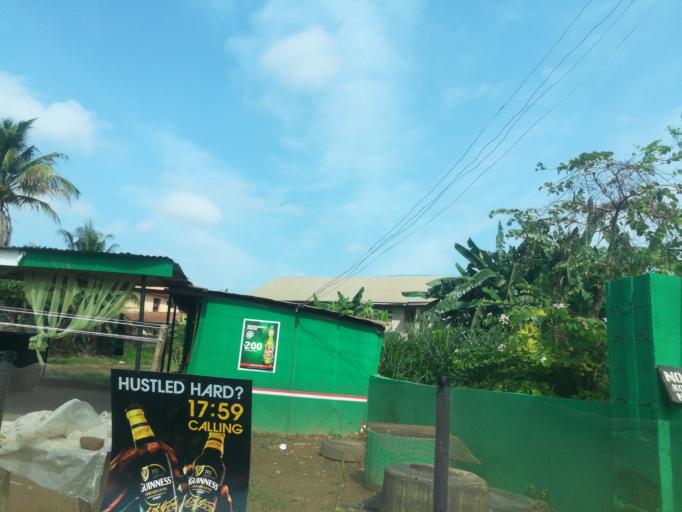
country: NG
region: Oyo
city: Ibadan
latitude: 7.3347
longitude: 3.8542
